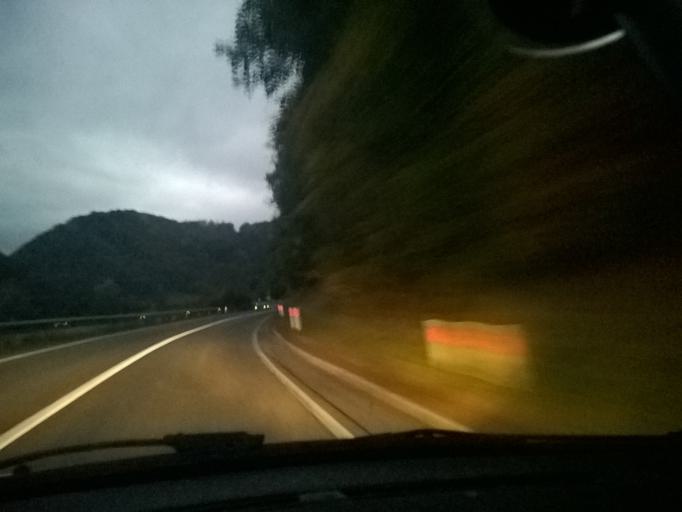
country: SI
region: Rogatec
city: Rogatec
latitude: 46.2217
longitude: 15.7460
